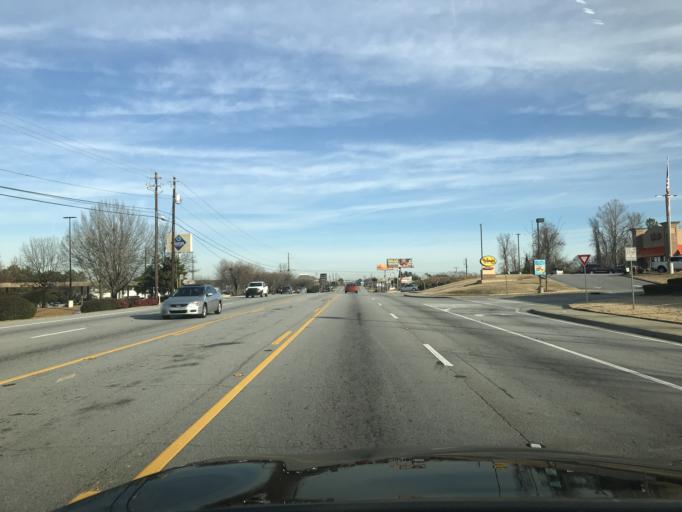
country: US
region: Georgia
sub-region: Clayton County
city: Morrow
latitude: 33.5539
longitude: -84.3471
